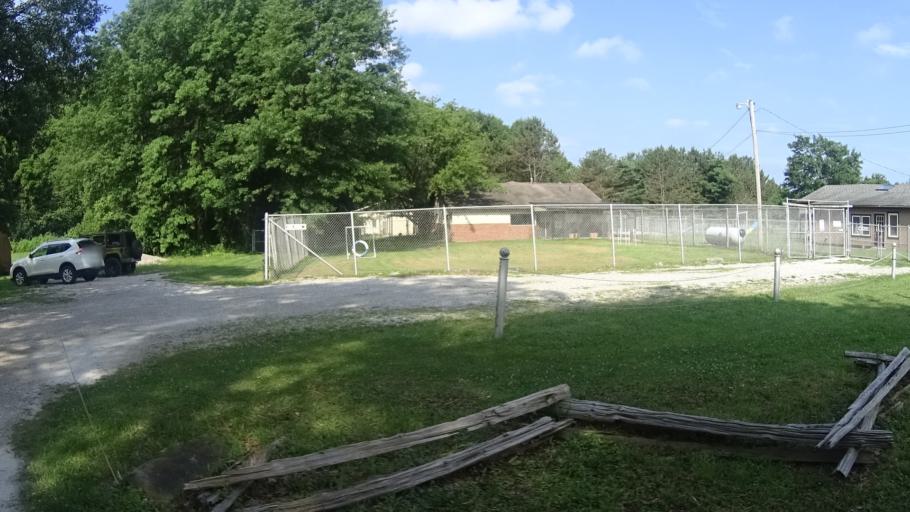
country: US
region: Ohio
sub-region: Lorain County
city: Vermilion
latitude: 41.3795
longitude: -82.4310
